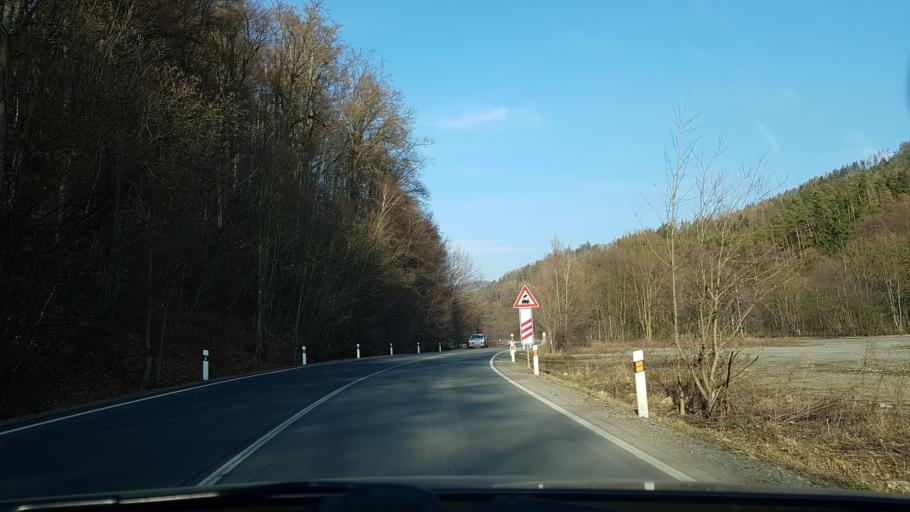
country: CZ
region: Olomoucky
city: Ruda nad Moravou
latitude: 49.9869
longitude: 16.8892
